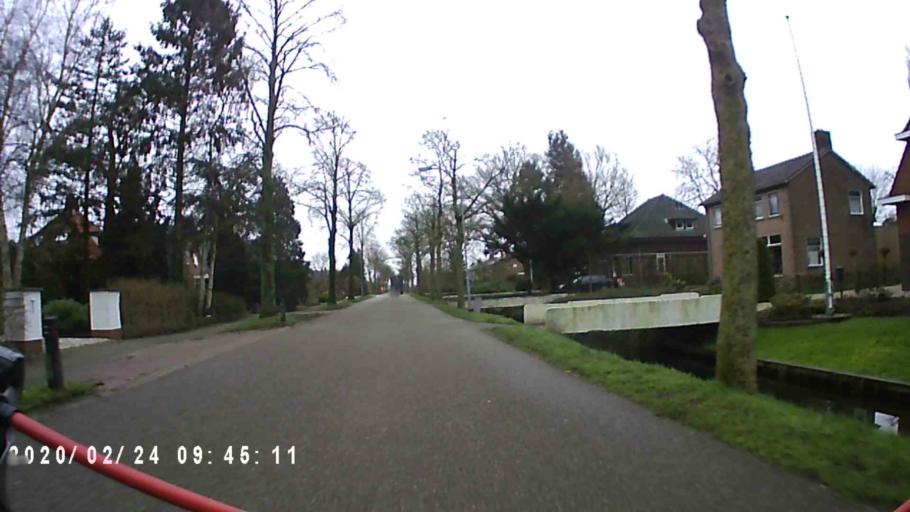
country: NL
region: Groningen
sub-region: Gemeente Winsum
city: Winsum
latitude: 53.2926
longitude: 6.5346
